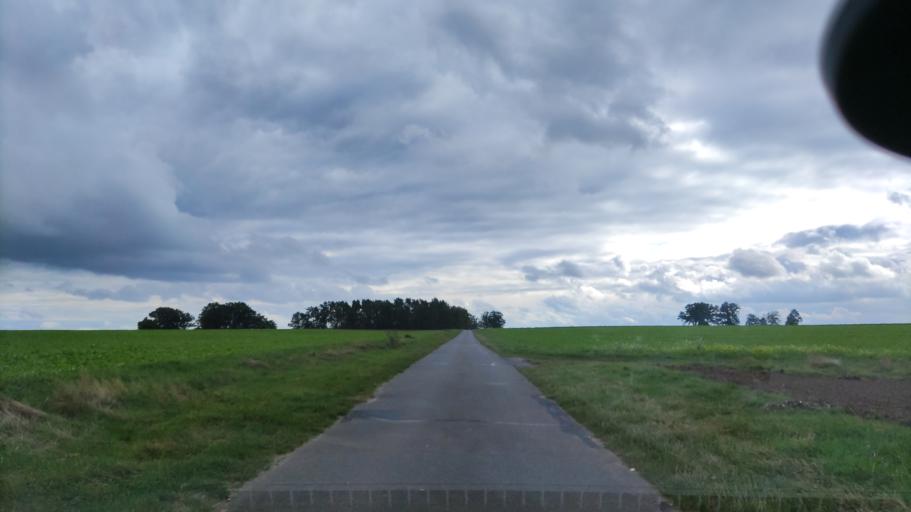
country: DE
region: Lower Saxony
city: Vastorf
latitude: 53.1615
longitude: 10.5334
